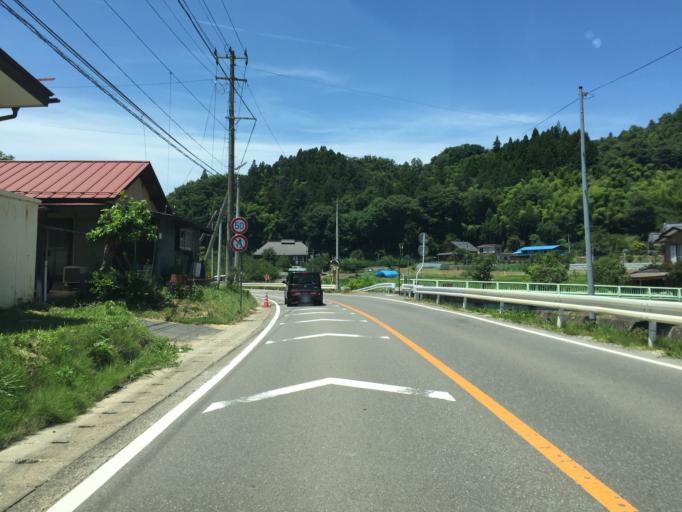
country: JP
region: Fukushima
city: Yanagawamachi-saiwaicho
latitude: 37.7616
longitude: 140.6283
